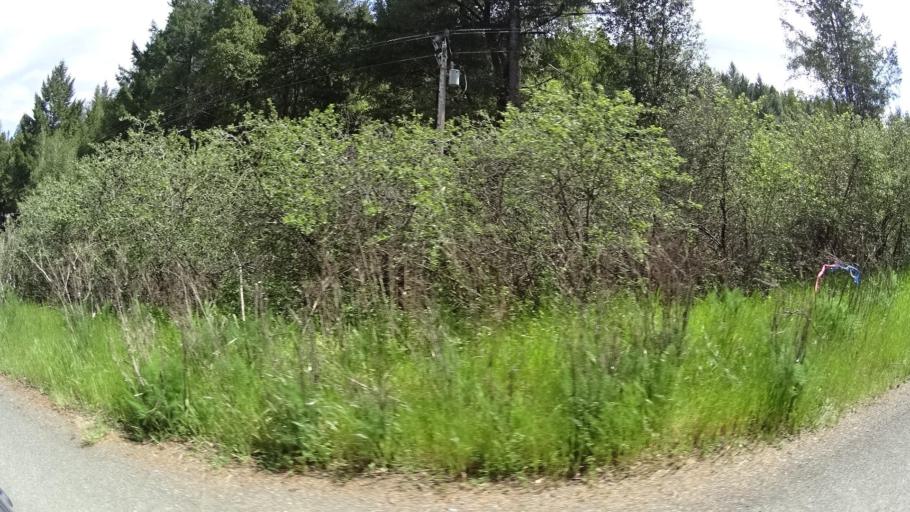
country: US
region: California
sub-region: Humboldt County
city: Redway
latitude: 40.0922
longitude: -123.9324
